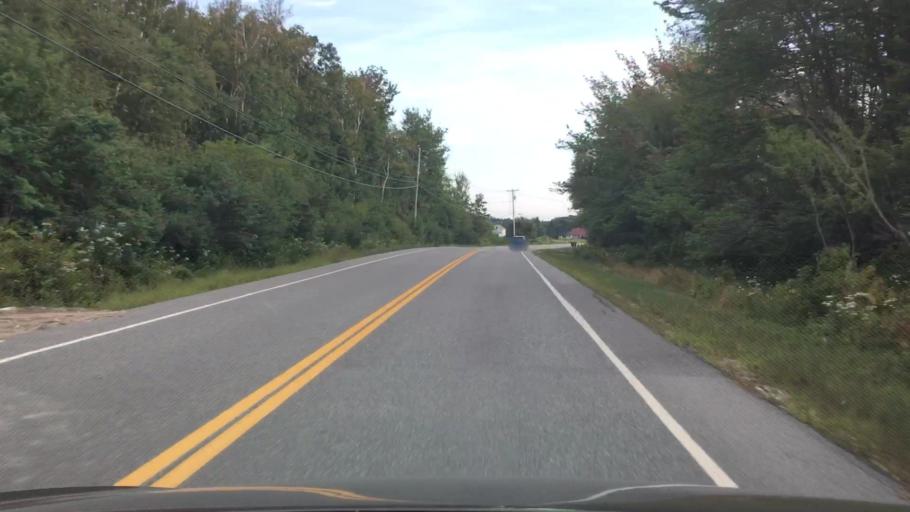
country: US
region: Maine
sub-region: Hancock County
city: Penobscot
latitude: 44.4681
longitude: -68.7817
